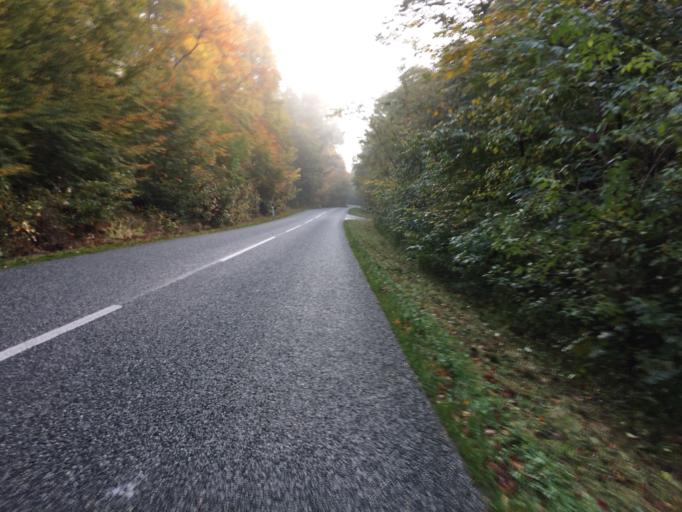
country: DK
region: Zealand
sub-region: Ringsted Kommune
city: Ringsted
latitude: 55.4896
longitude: 11.8025
